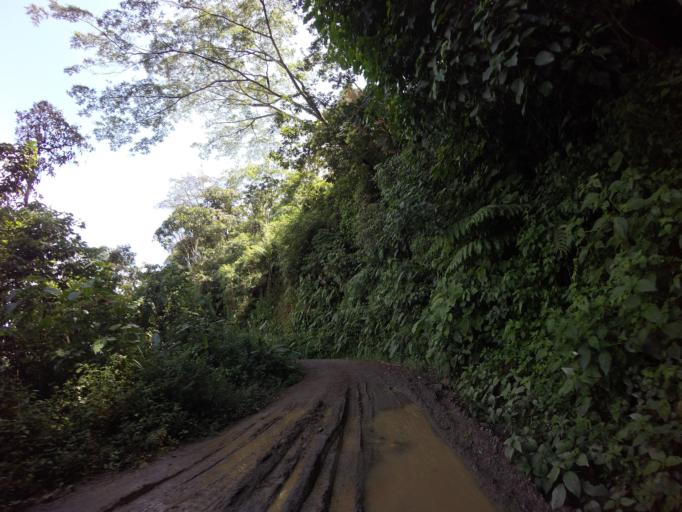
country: CO
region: Antioquia
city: Narino
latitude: 5.5156
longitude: -75.1828
